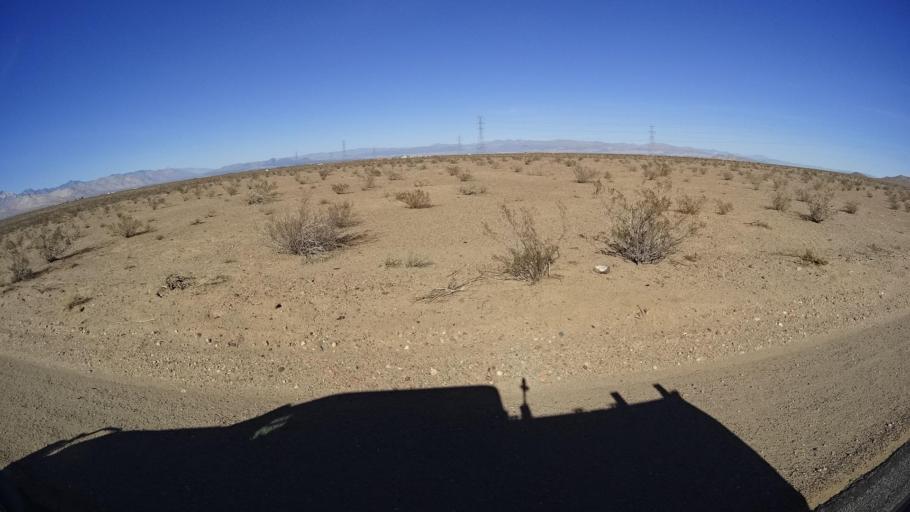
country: US
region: California
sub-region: Kern County
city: China Lake Acres
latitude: 35.5600
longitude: -117.7641
